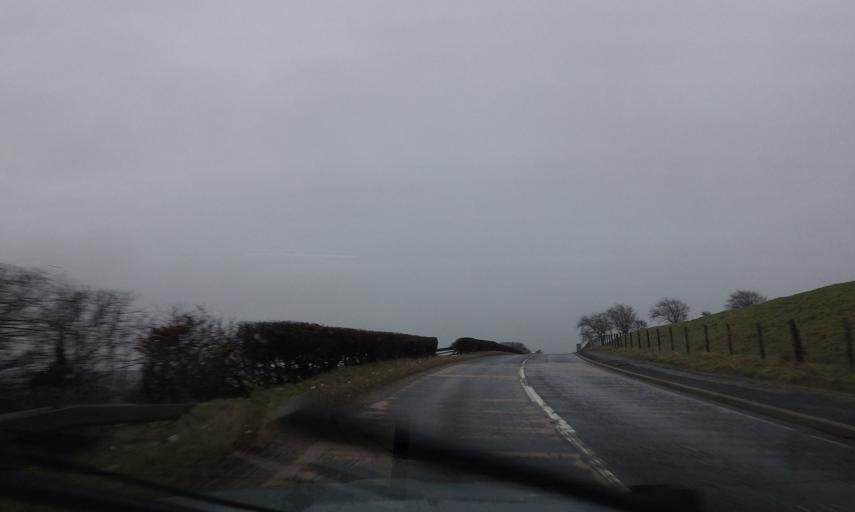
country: GB
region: Scotland
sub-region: North Lanarkshire
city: Shotts
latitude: 55.8087
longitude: -3.8088
